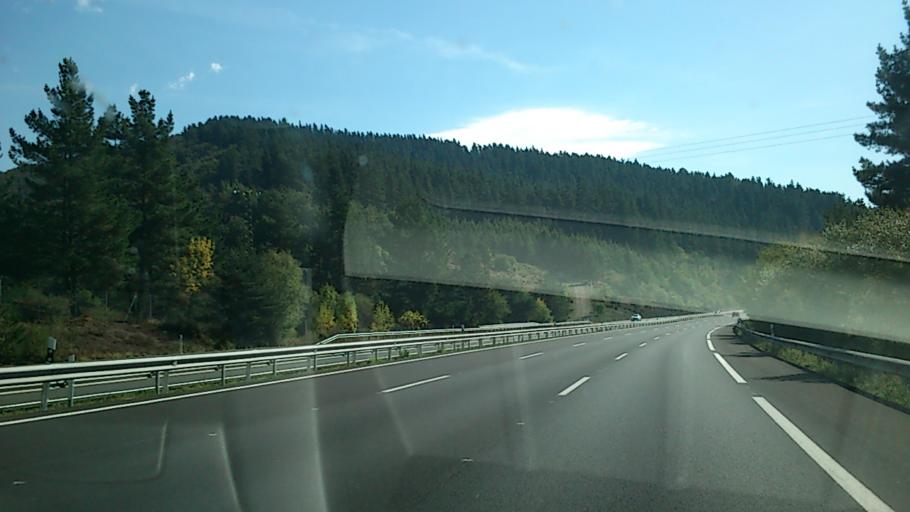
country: ES
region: Basque Country
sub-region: Provincia de Alava
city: Lezama
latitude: 43.0344
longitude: -2.9151
